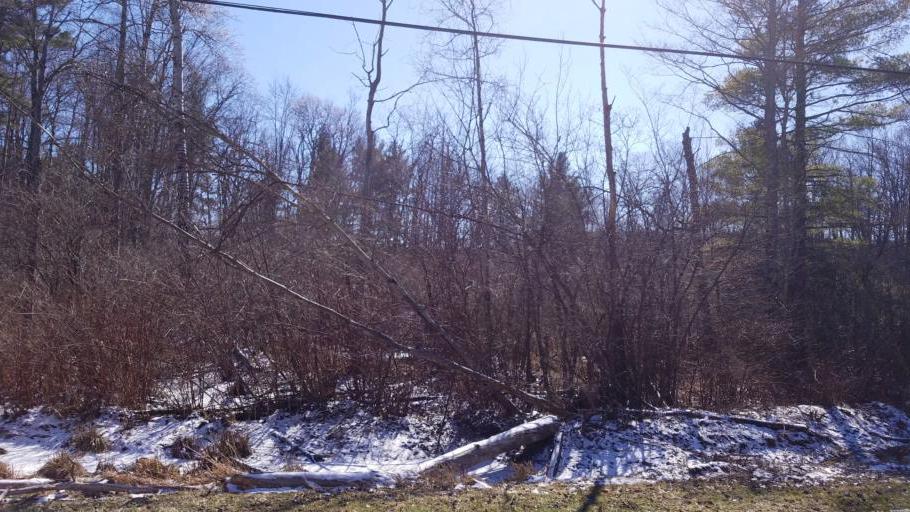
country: US
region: New York
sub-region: Allegany County
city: Wellsville
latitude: 42.0485
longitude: -77.9216
